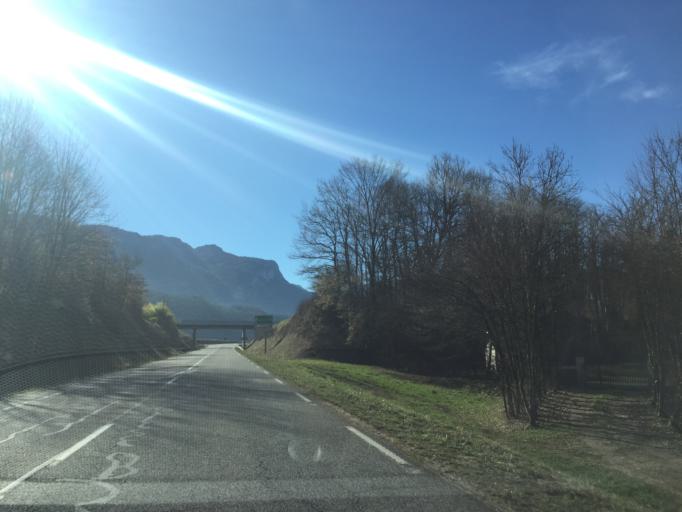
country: FR
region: Rhone-Alpes
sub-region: Departement de la Savoie
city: Les Echelles
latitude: 45.4383
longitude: 5.7655
